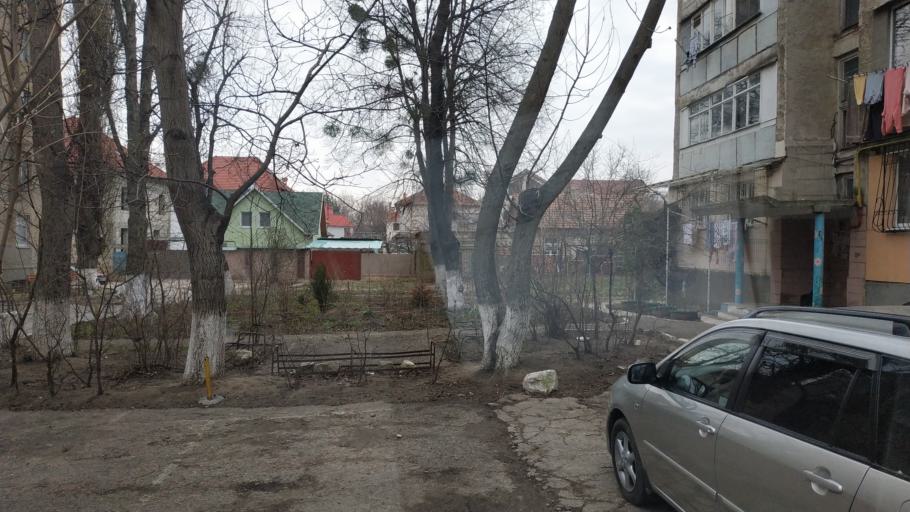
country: MD
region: Chisinau
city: Vatra
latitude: 47.0321
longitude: 28.7870
